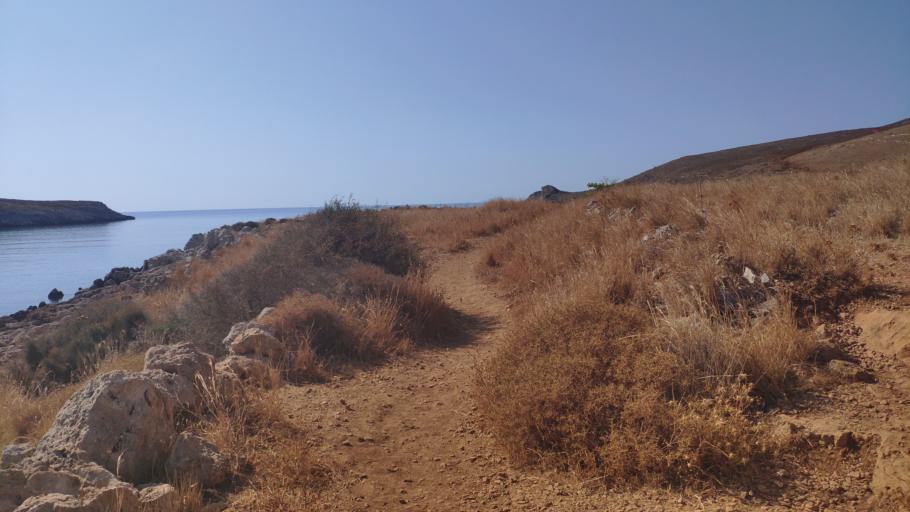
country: GR
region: Peloponnese
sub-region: Nomos Lakonias
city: Gytheio
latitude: 36.4010
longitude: 22.4853
